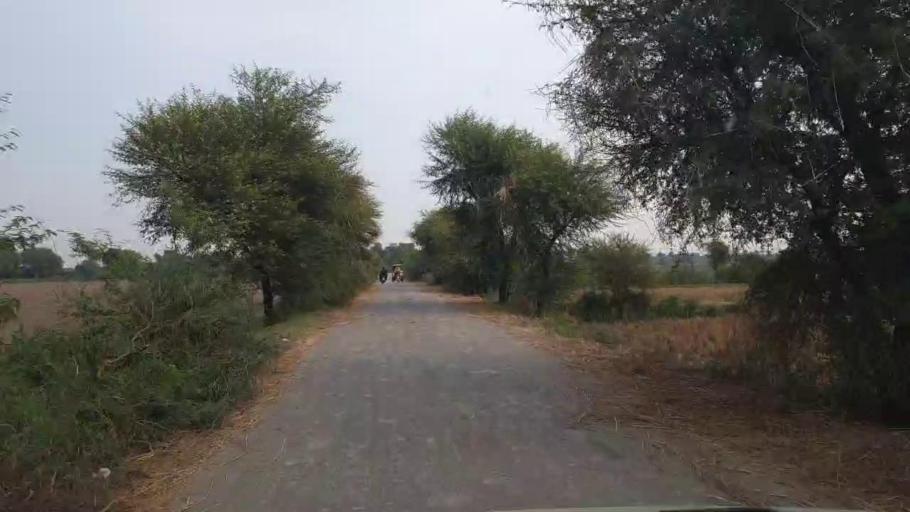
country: PK
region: Sindh
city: Talhar
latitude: 24.8966
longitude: 68.8053
